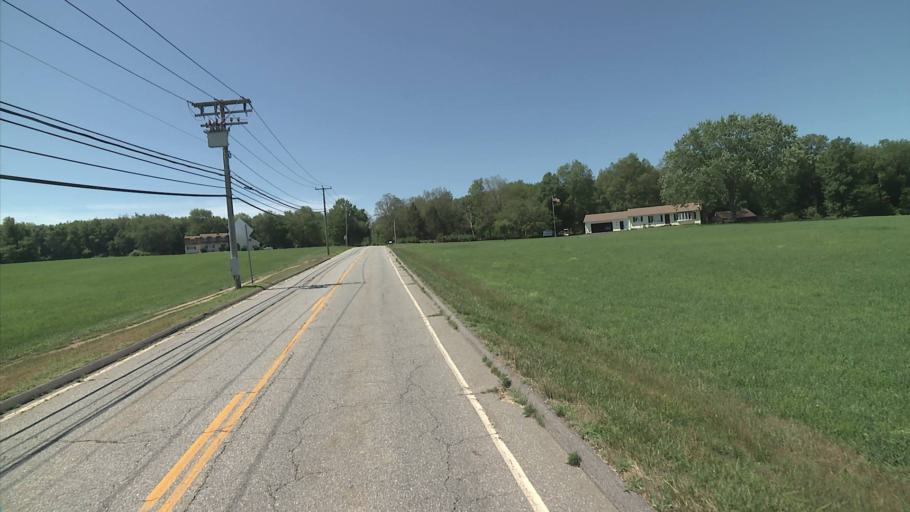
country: US
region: Connecticut
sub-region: New London County
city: Colchester
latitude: 41.6153
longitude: -72.2727
